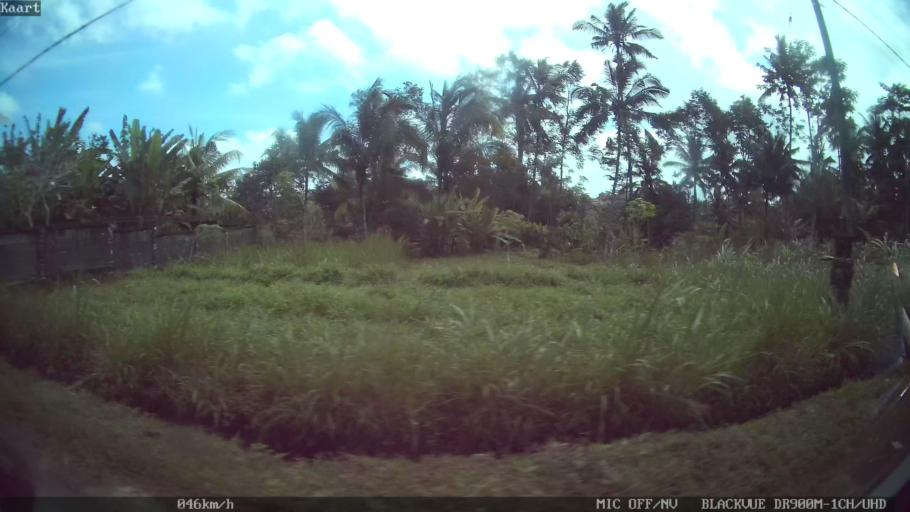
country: ID
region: Bali
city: Banjar Bebalang
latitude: -8.4747
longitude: 115.3421
